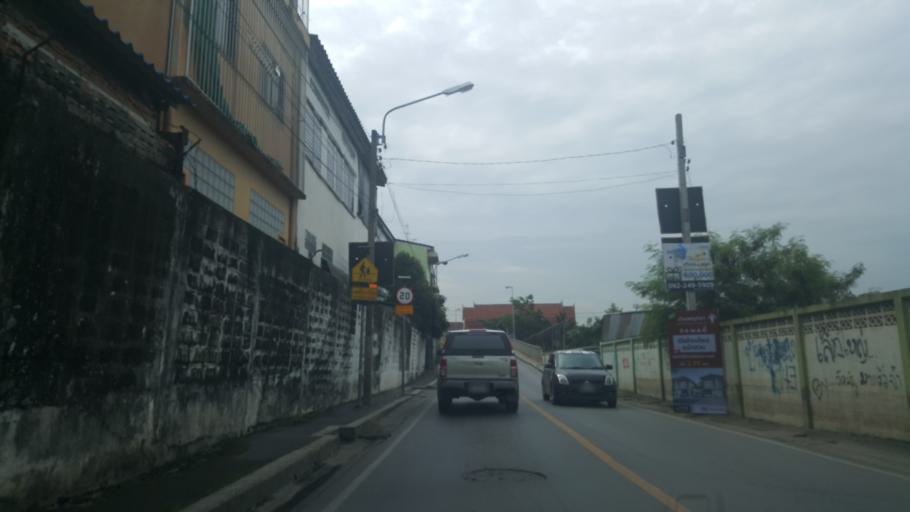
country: TH
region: Bangkok
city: Bang Khae
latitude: 13.6962
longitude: 100.3914
